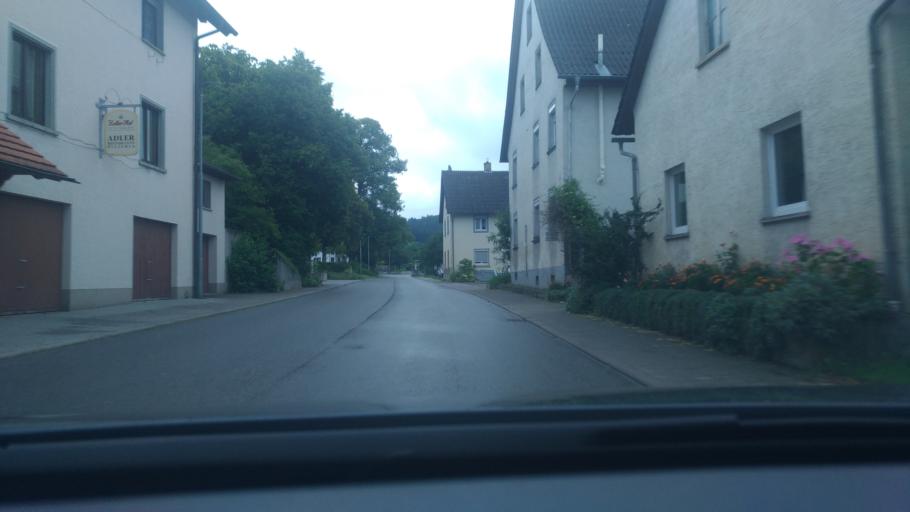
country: DE
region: Baden-Wuerttemberg
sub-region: Tuebingen Region
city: Sipplingen
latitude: 47.8169
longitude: 9.1167
